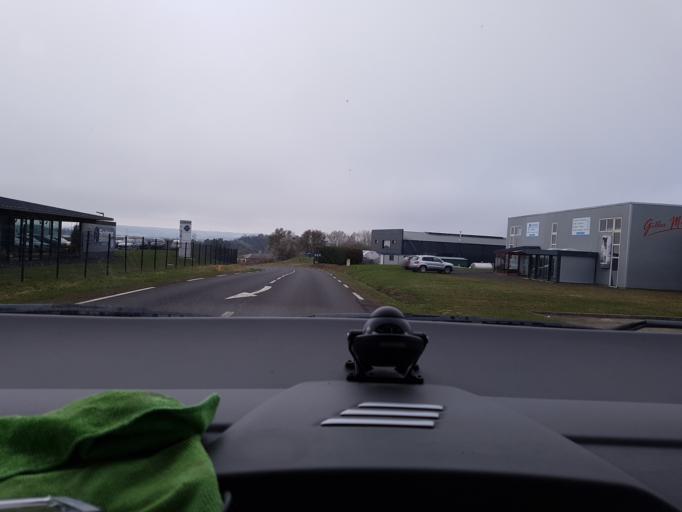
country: FR
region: Auvergne
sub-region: Departement du Cantal
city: Saint-Flour
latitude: 45.0598
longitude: 3.1078
